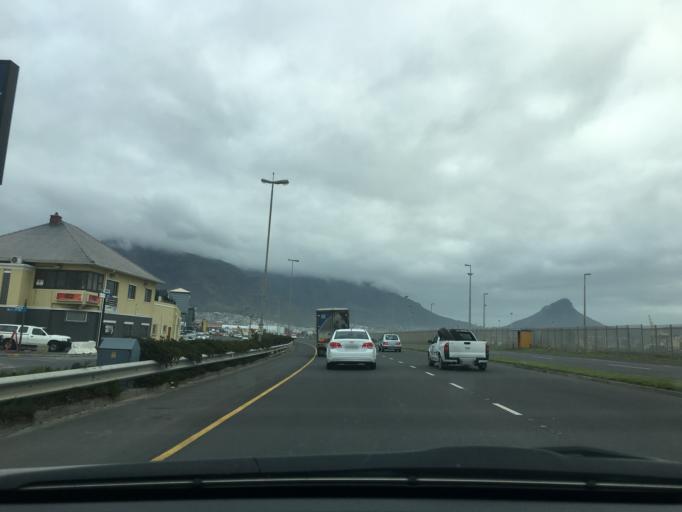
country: ZA
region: Western Cape
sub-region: City of Cape Town
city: Rosebank
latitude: -33.9105
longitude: 18.4701
